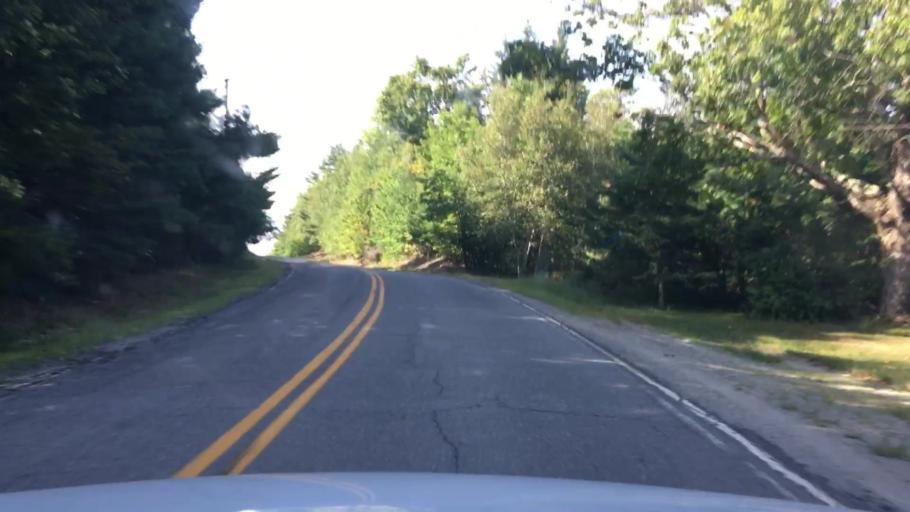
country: US
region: Maine
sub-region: Penobscot County
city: Enfield
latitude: 45.2092
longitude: -68.5223
